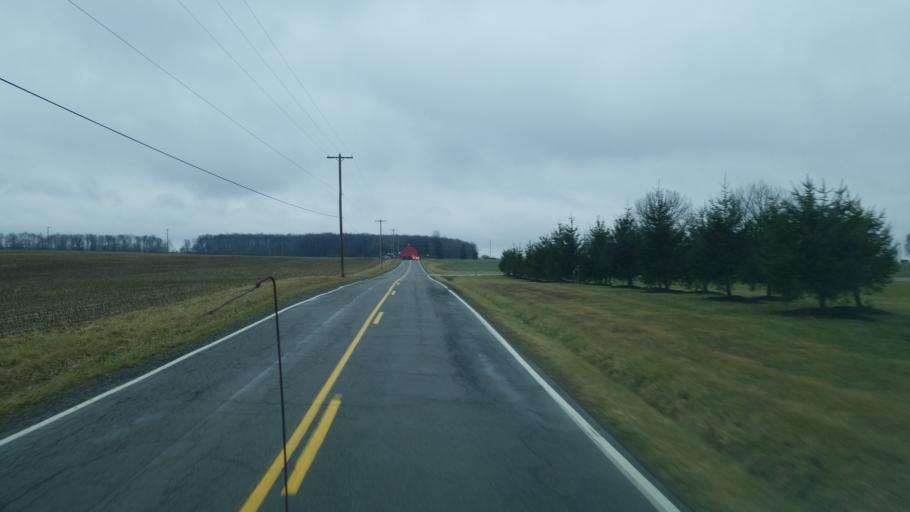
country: US
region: Ohio
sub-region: Wayne County
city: Orrville
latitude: 40.9051
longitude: -81.7823
